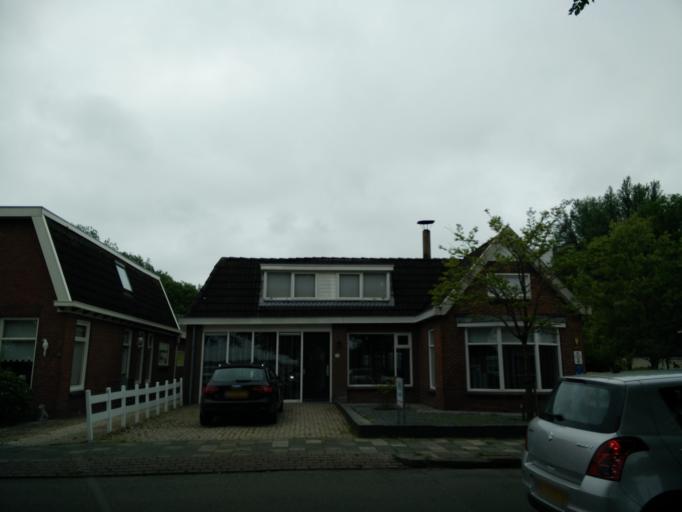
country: NL
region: Groningen
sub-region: Gemeente Zuidhorn
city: Aduard
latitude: 53.2198
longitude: 6.5005
